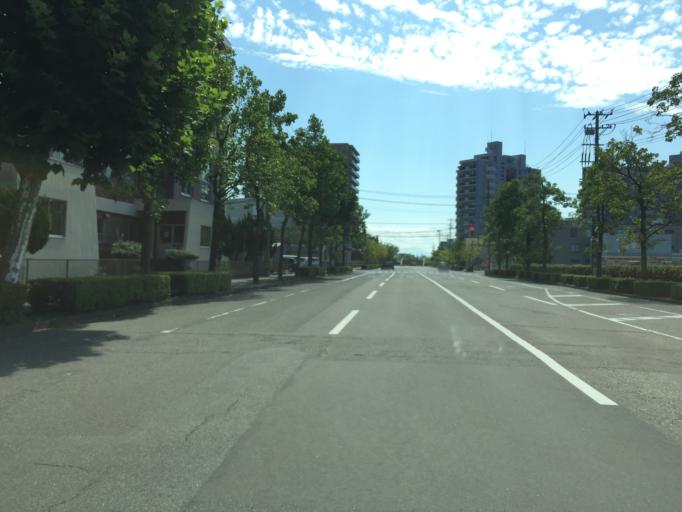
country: JP
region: Niigata
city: Niigata-shi
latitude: 37.9115
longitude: 139.0316
